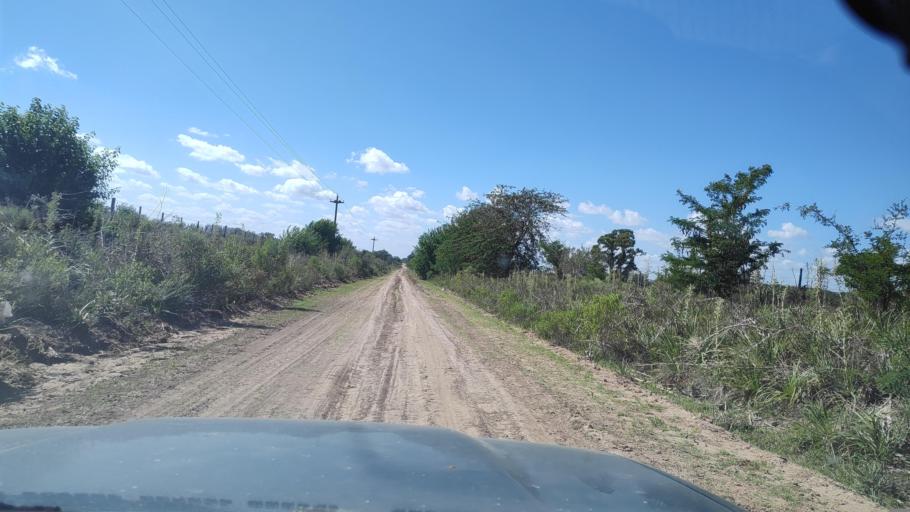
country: AR
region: Buenos Aires
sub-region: Partido de Lujan
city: Lujan
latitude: -34.5177
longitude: -59.1612
